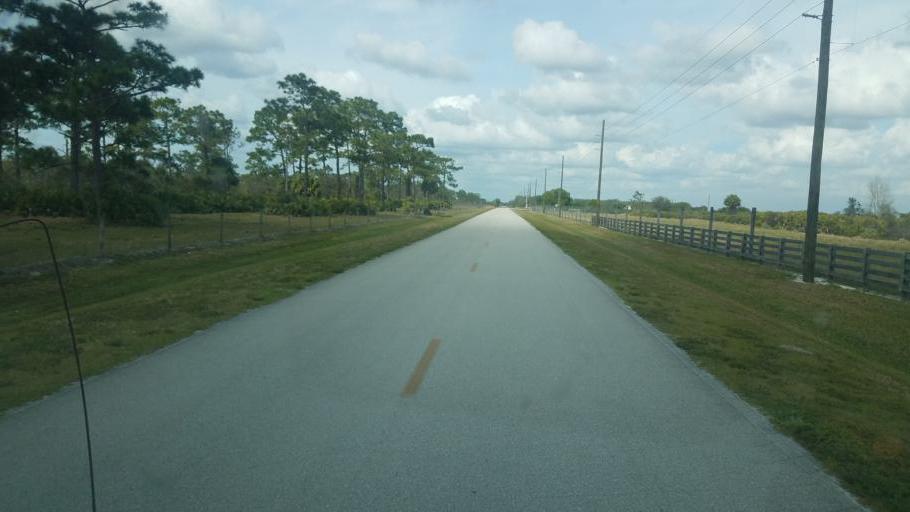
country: US
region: Florida
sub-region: Okeechobee County
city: Cypress Quarters
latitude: 27.4978
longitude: -80.7746
